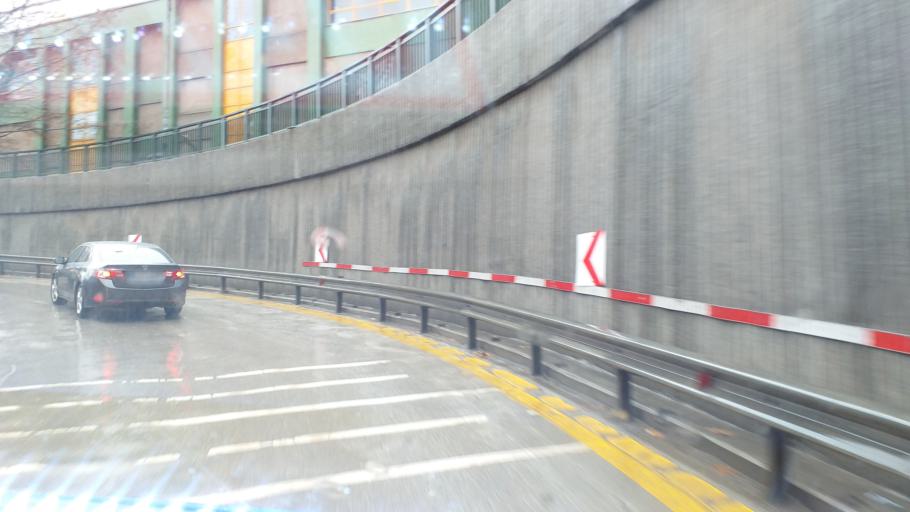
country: TR
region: Ankara
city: Ankara
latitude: 39.9574
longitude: 32.8172
